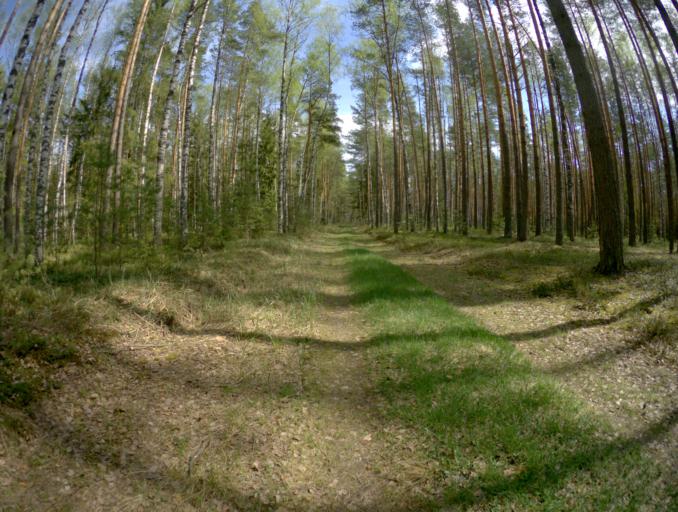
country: RU
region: Vladimir
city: Golovino
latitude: 55.9298
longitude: 40.3754
